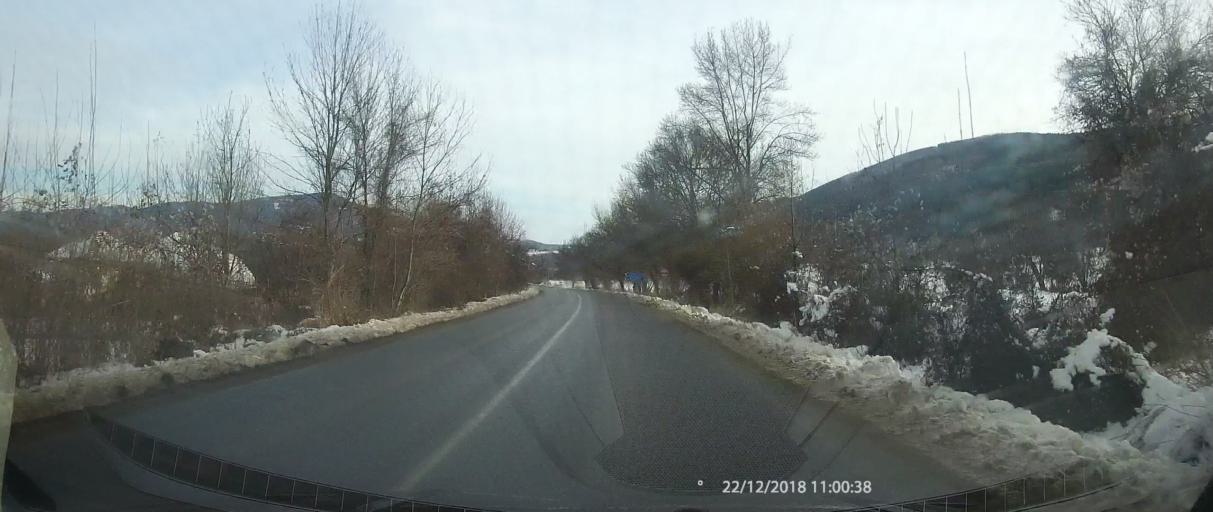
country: MK
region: Kriva Palanka
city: Kriva Palanka
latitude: 42.2356
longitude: 22.5035
